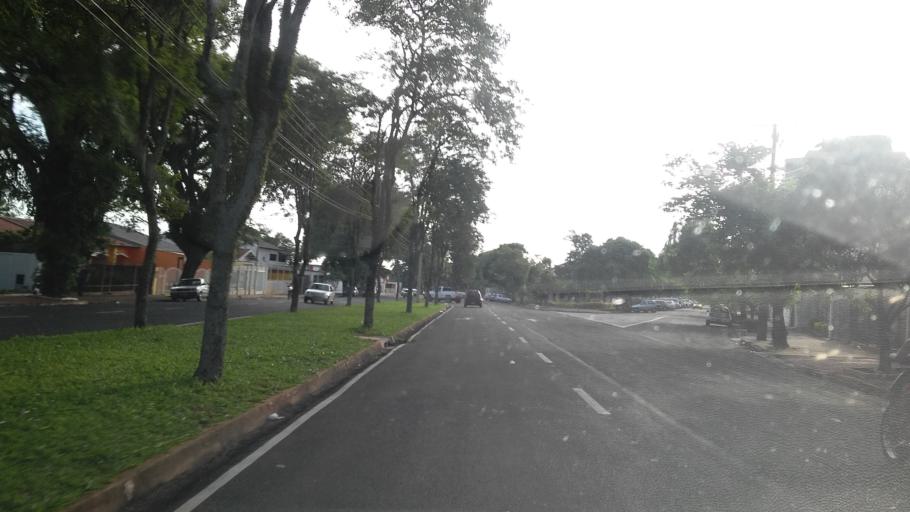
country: BR
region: Parana
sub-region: Londrina
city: Londrina
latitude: -23.3006
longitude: -51.1774
